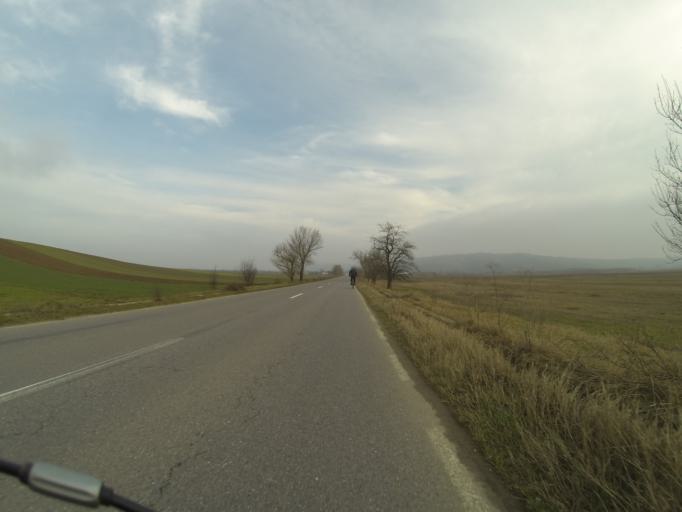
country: RO
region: Mehedinti
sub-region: Comuna Corlatel
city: Corlatel
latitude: 44.3994
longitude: 22.9176
